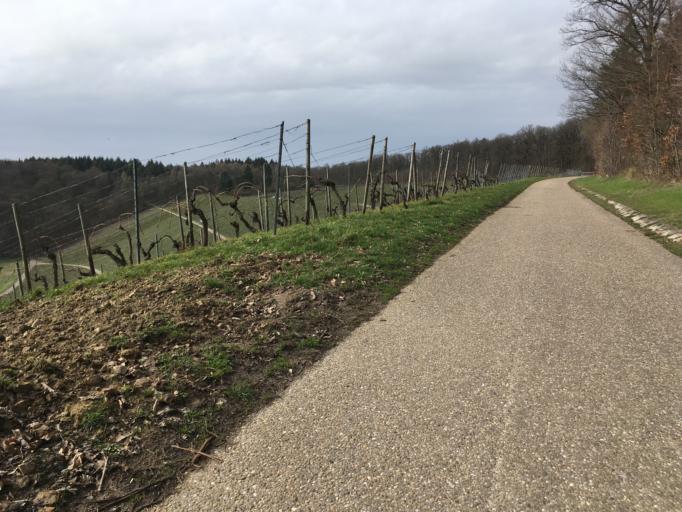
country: DE
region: Baden-Wuerttemberg
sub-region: Regierungsbezirk Stuttgart
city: Leingarten
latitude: 49.1240
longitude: 9.0944
